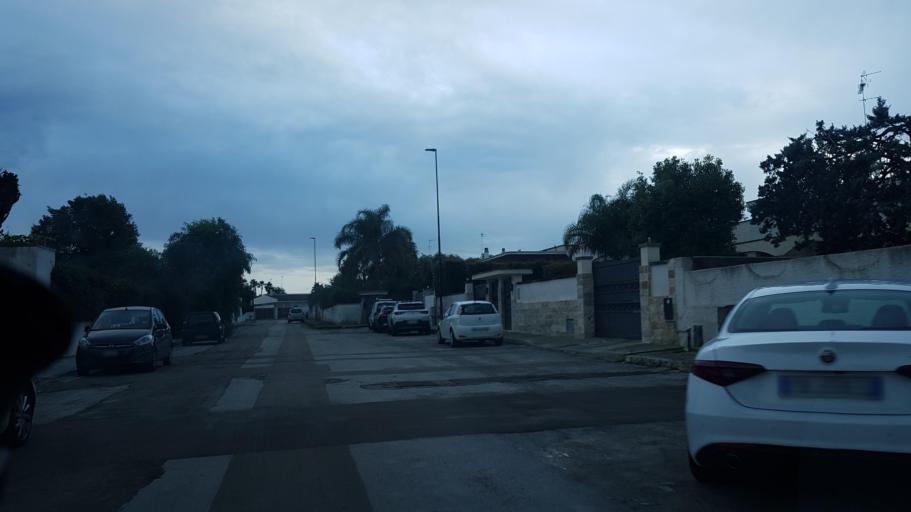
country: IT
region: Apulia
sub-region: Provincia di Lecce
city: Merine
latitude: 40.3389
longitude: 18.2176
